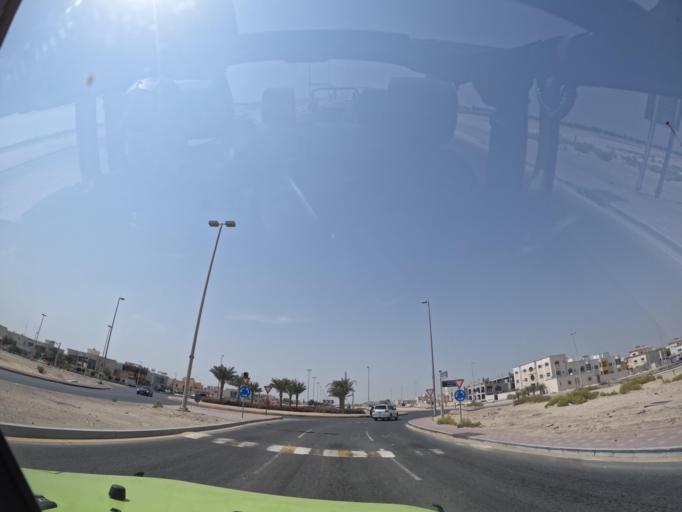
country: AE
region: Abu Dhabi
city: Abu Dhabi
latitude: 24.3432
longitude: 54.6325
